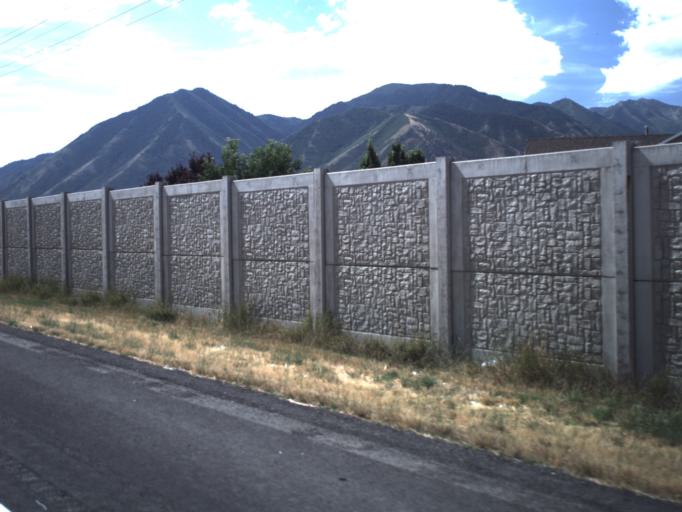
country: US
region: Utah
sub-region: Utah County
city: Spanish Fork
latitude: 40.1047
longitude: -111.6226
